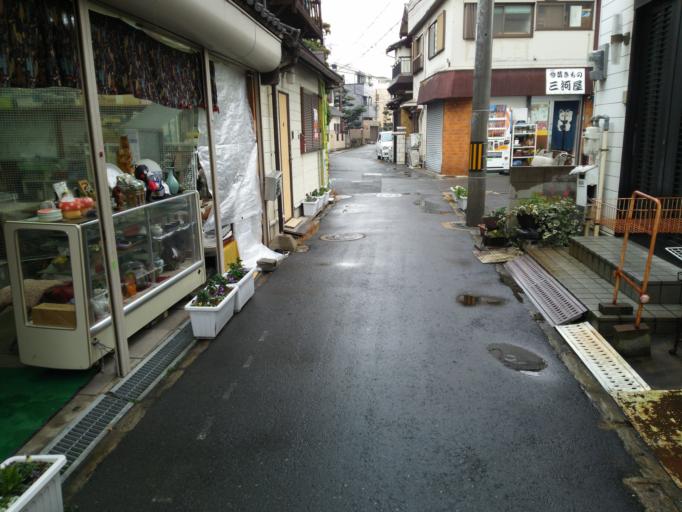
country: JP
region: Hyogo
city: Itami
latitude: 34.7541
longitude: 135.4162
